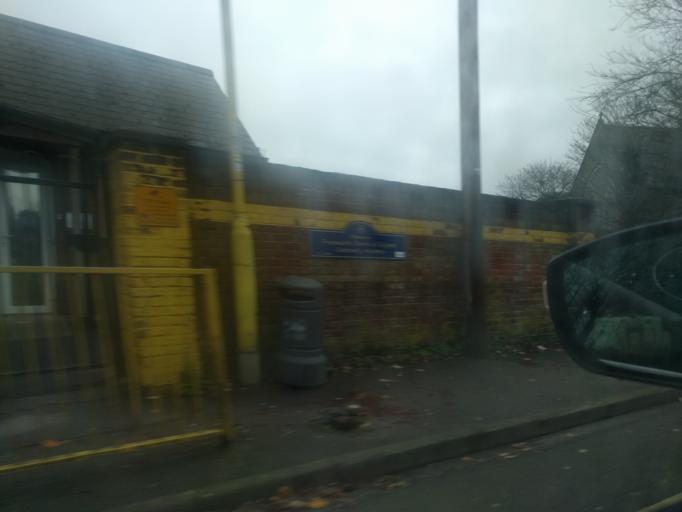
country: GB
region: England
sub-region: Southampton
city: Southampton
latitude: 50.9119
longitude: -1.4272
